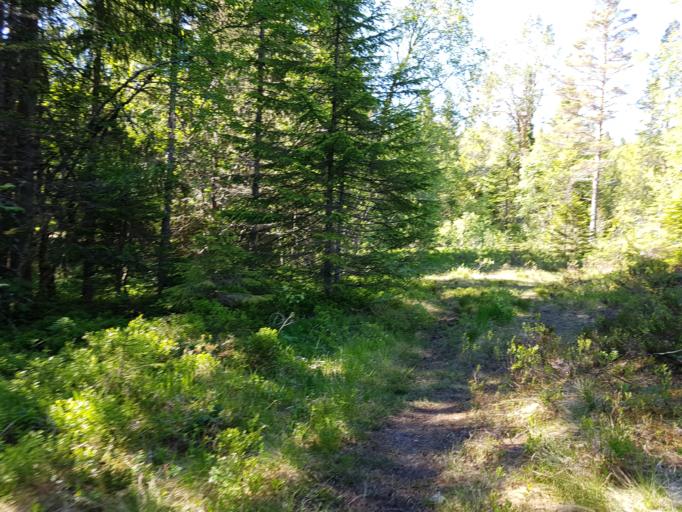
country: NO
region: Sor-Trondelag
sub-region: Trondheim
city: Trondheim
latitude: 63.4082
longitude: 10.3161
